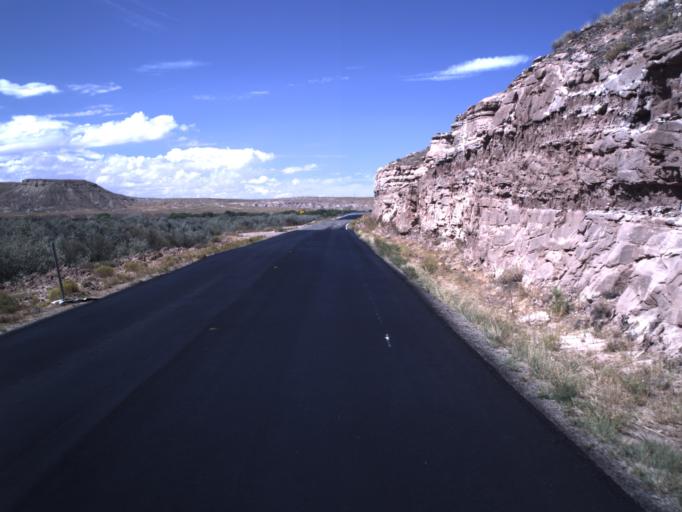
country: US
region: Utah
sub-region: San Juan County
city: Blanding
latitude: 37.2575
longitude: -109.2839
